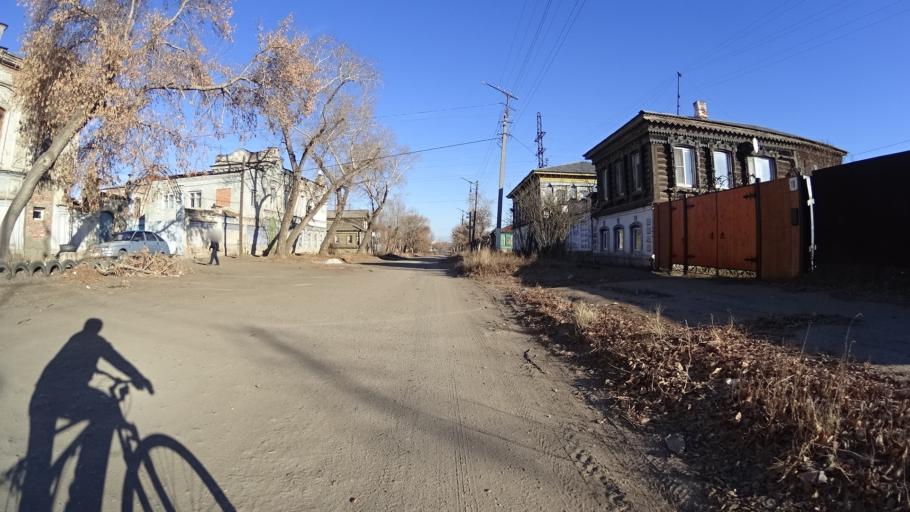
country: RU
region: Chelyabinsk
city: Troitsk
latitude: 54.0826
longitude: 61.5652
